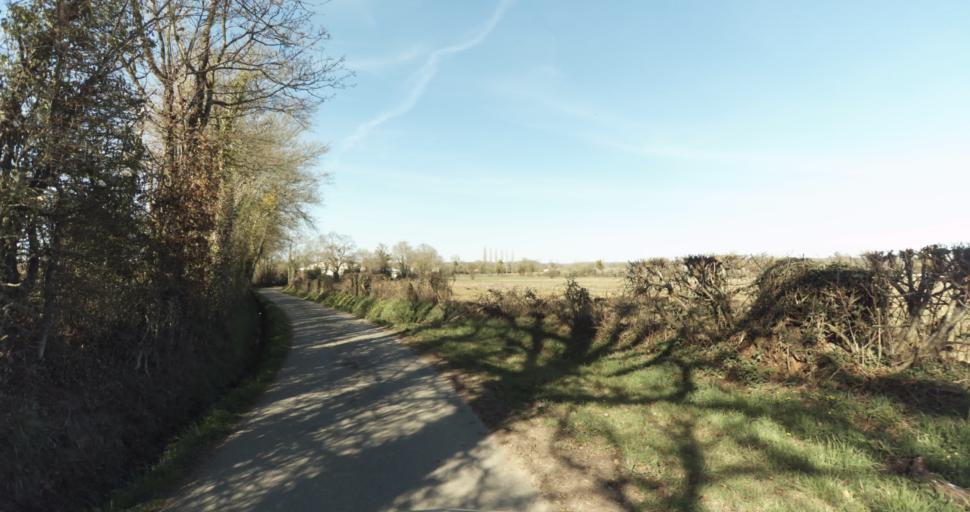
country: FR
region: Lower Normandy
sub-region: Departement du Calvados
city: Saint-Pierre-sur-Dives
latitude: 49.0489
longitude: 0.0544
